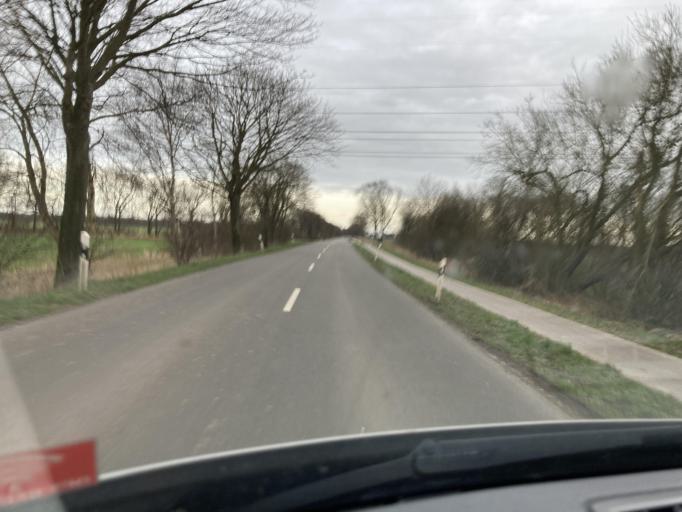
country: DE
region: Lower Saxony
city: Leer
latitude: 53.1736
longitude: 7.4250
